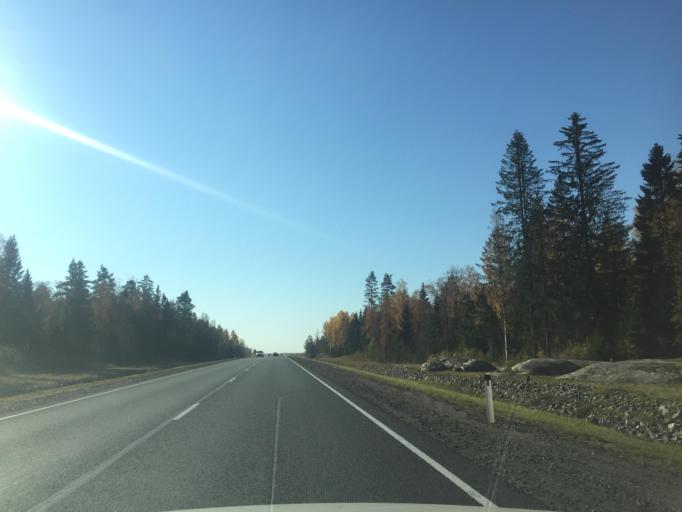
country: RU
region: Leningrad
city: Kuznechnoye
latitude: 61.3599
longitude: 29.8919
